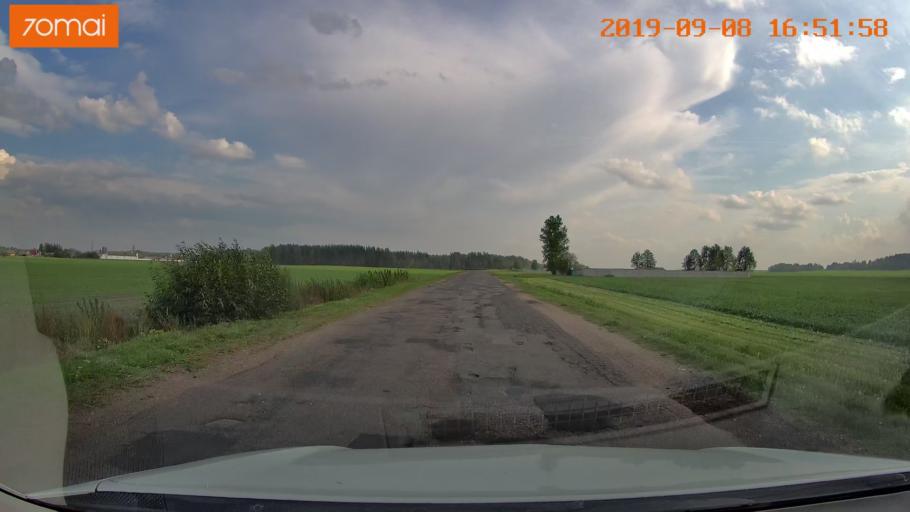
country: BY
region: Grodnenskaya
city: Hrodna
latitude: 53.7800
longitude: 23.8989
